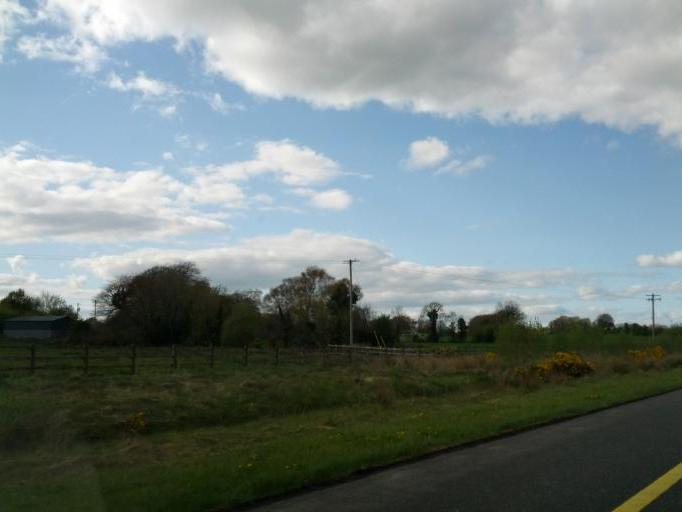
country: IE
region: Leinster
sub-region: An Iarmhi
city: Athlone
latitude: 53.3575
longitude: -8.0637
